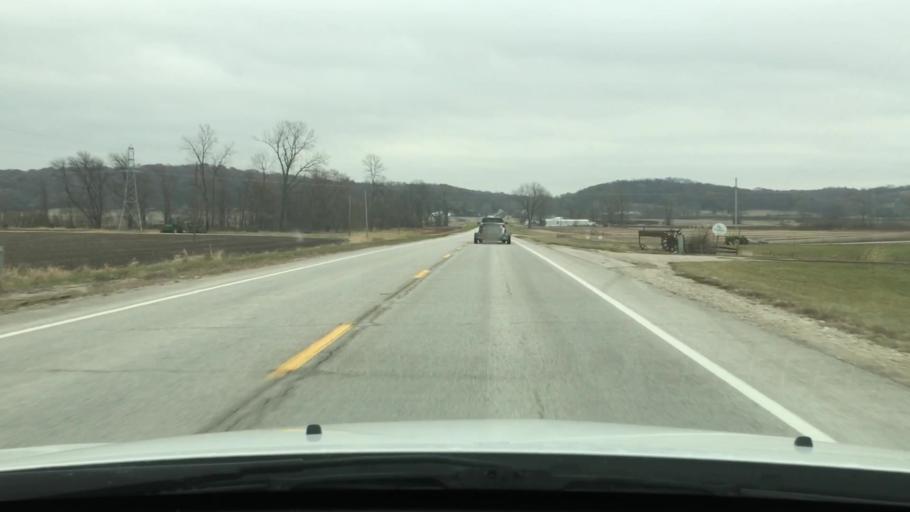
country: US
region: Missouri
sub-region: Pike County
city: Louisiana
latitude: 39.5066
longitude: -90.9835
